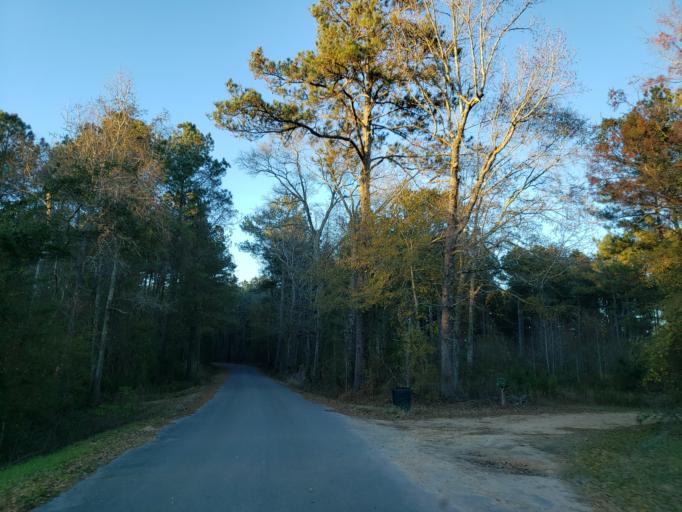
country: US
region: Mississippi
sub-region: Covington County
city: Collins
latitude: 31.5694
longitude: -89.4390
